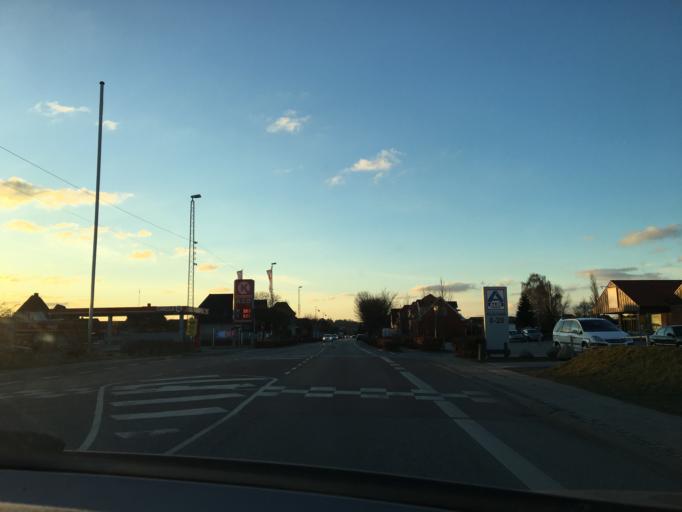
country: DK
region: South Denmark
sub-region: Middelfart Kommune
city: Middelfart
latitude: 55.5014
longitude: 9.7493
